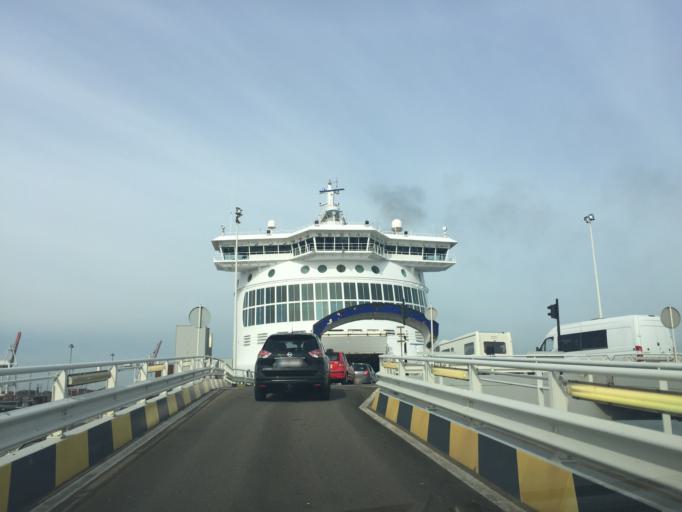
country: FR
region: Nord-Pas-de-Calais
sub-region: Departement du Nord
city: Loon-Plage
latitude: 51.0203
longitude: 2.1904
